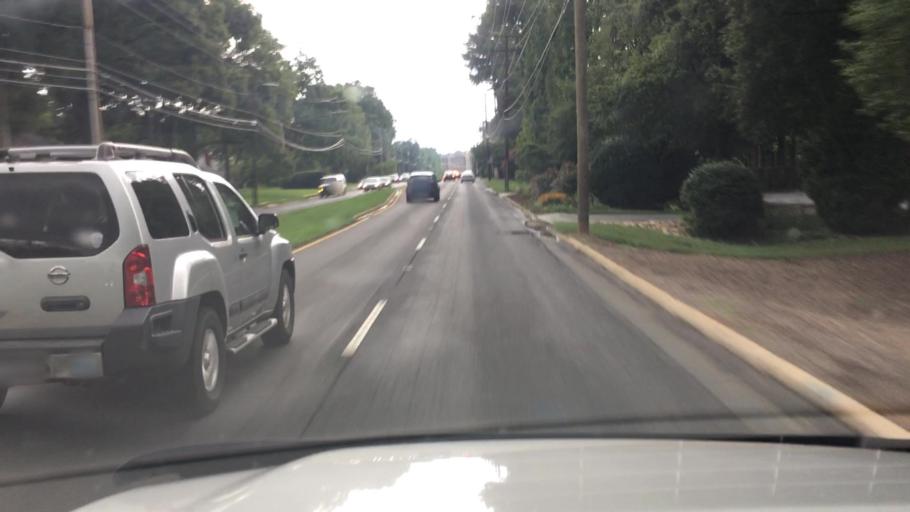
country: US
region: North Carolina
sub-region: Mecklenburg County
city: Charlotte
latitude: 35.1641
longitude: -80.8022
